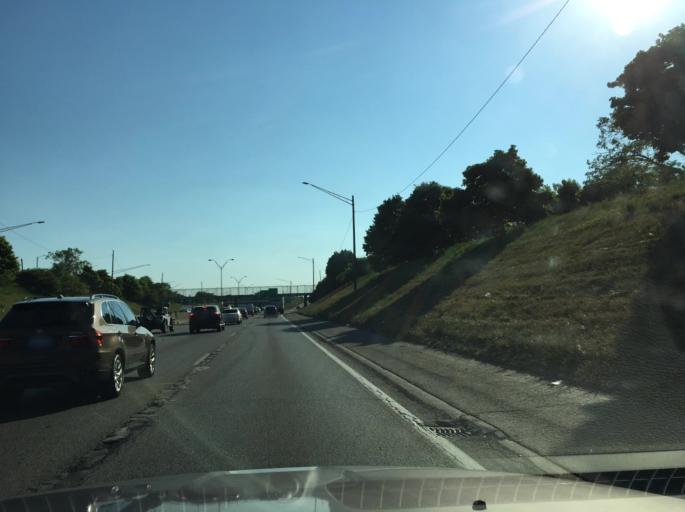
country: US
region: Michigan
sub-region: Wayne County
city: Hamtramck
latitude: 42.3884
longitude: -83.0149
